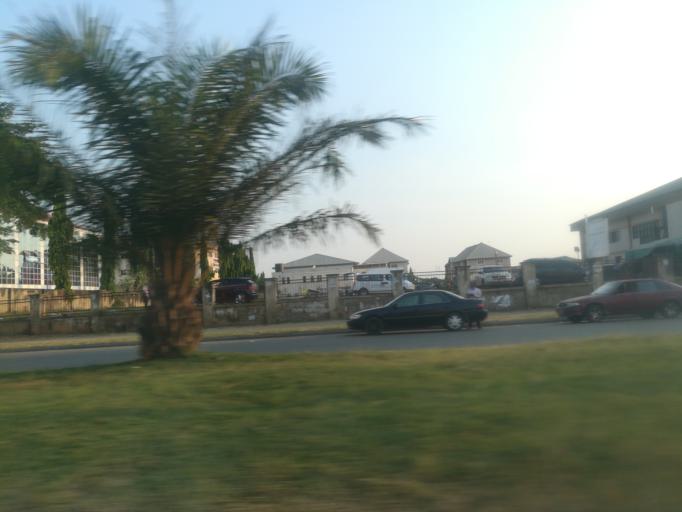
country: NG
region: Abuja Federal Capital Territory
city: Abuja
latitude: 9.0679
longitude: 7.4412
